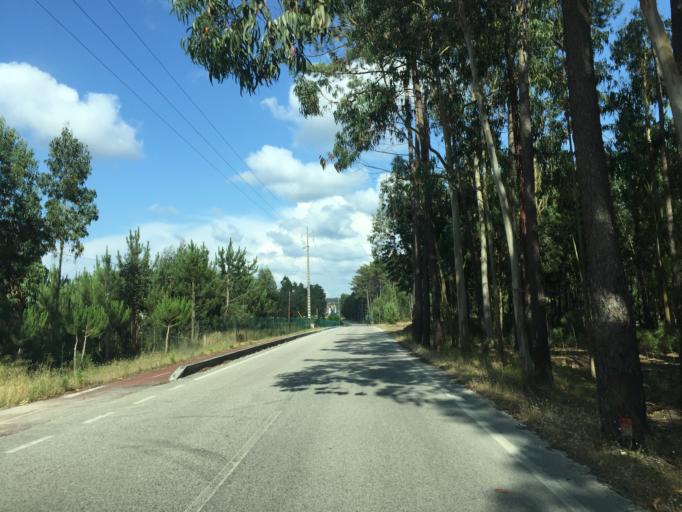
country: PT
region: Leiria
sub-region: Leiria
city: Monte Redondo
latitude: 39.9437
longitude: -8.8181
